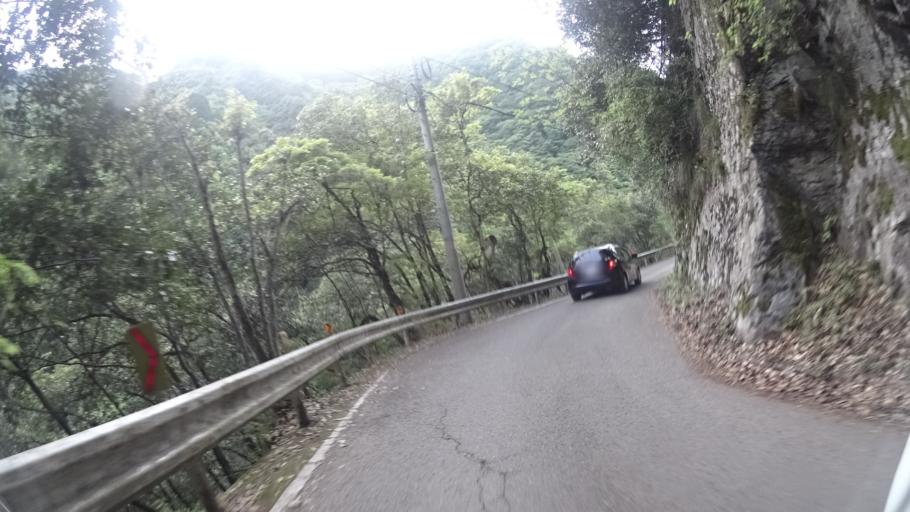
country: JP
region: Tokushima
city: Ikedacho
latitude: 33.9417
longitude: 133.8079
